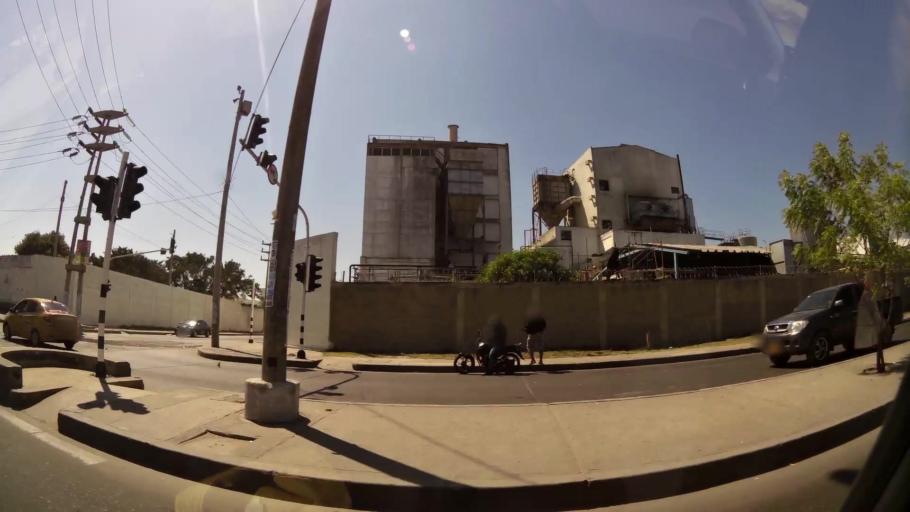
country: CO
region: Atlantico
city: Barranquilla
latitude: 10.9541
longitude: -74.7739
